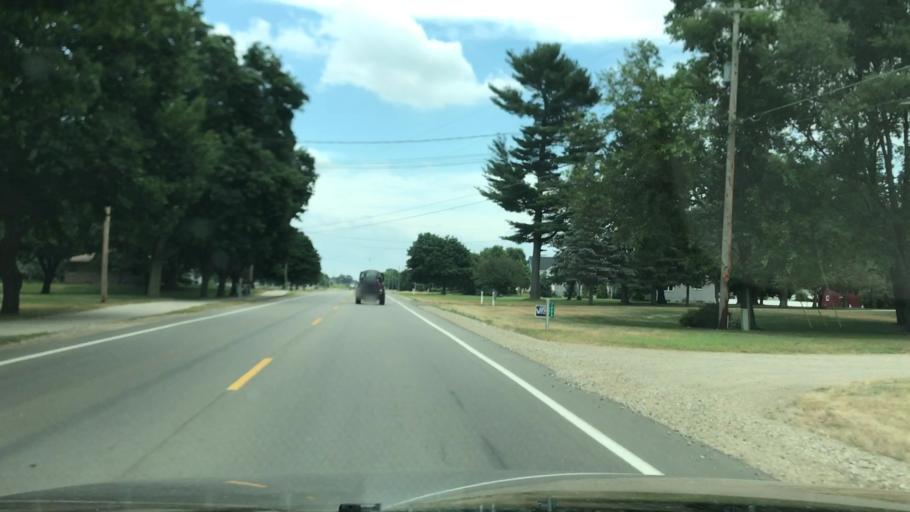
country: US
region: Michigan
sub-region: Ottawa County
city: Zeeland
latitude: 42.7833
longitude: -85.9777
